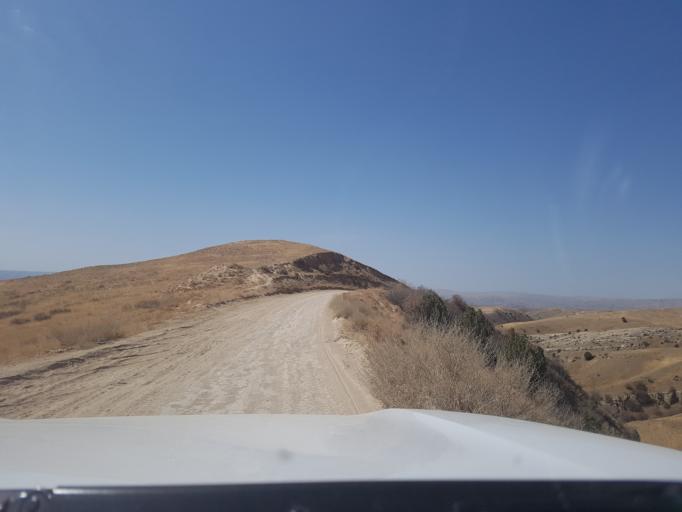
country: TM
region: Ahal
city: Baharly
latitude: 38.2747
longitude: 56.9021
